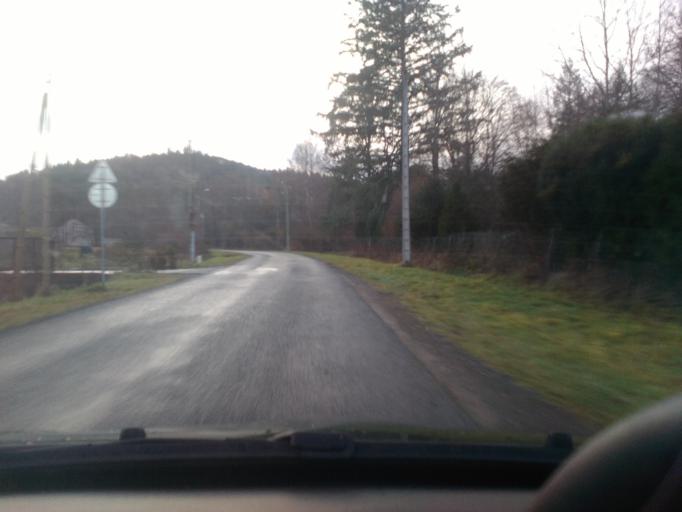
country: FR
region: Lorraine
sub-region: Departement des Vosges
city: Saint-Leonard
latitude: 48.2165
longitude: 6.9388
